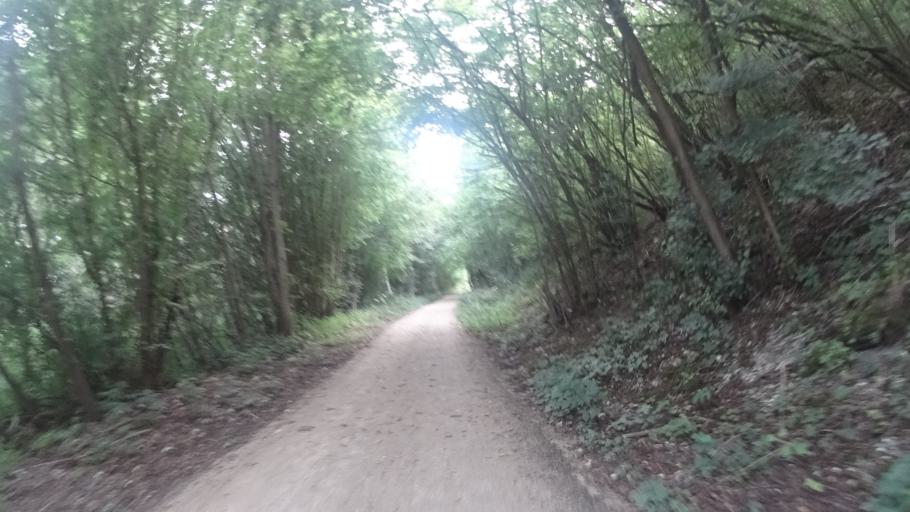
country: FR
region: Picardie
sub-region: Departement de l'Aisne
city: Origny-Sainte-Benoite
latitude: 49.8719
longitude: 3.5308
